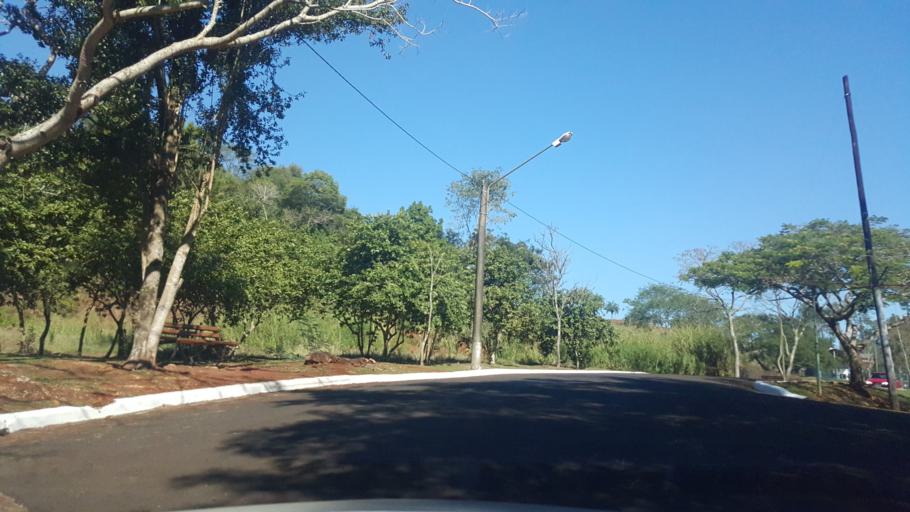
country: AR
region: Misiones
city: Puerto Rico
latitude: -26.7922
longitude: -55.0265
